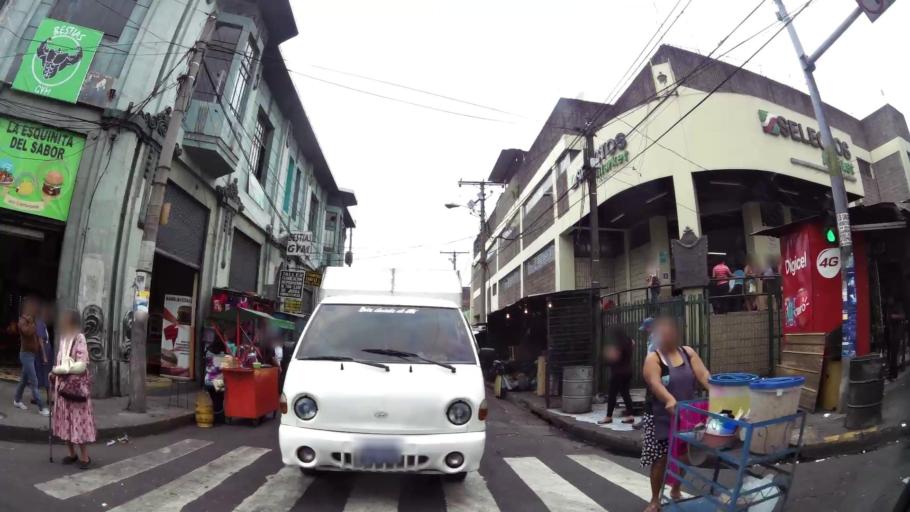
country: SV
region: San Salvador
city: San Salvador
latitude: 13.6995
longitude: -89.1888
